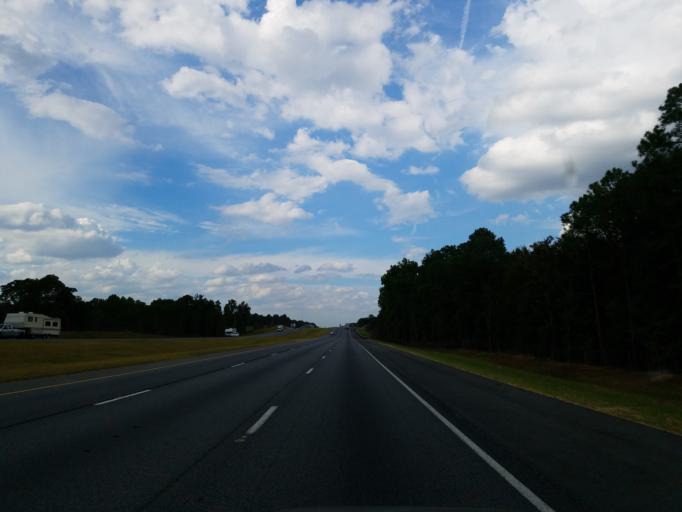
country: US
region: Georgia
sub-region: Crisp County
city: Cordele
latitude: 31.8843
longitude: -83.7289
